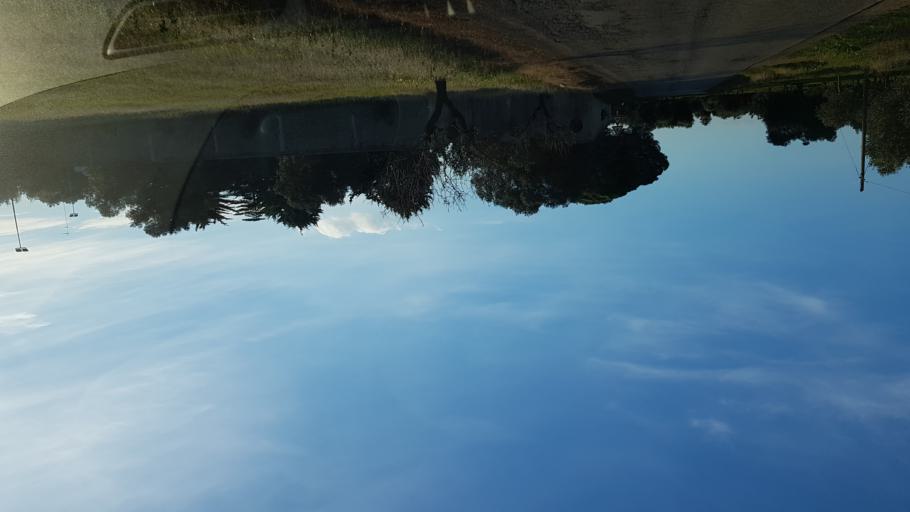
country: IT
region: Apulia
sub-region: Provincia di Brindisi
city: San Vito dei Normanni
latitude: 40.6728
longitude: 17.7768
